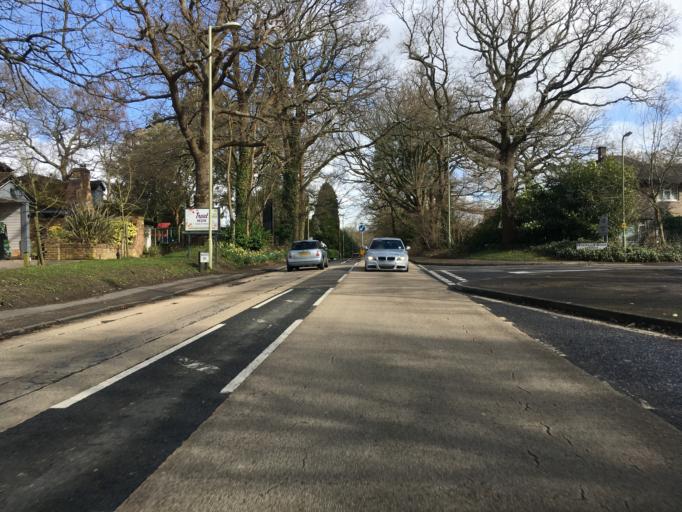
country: GB
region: England
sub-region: Hampshire
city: Chandlers Ford
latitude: 50.9894
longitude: -1.3713
